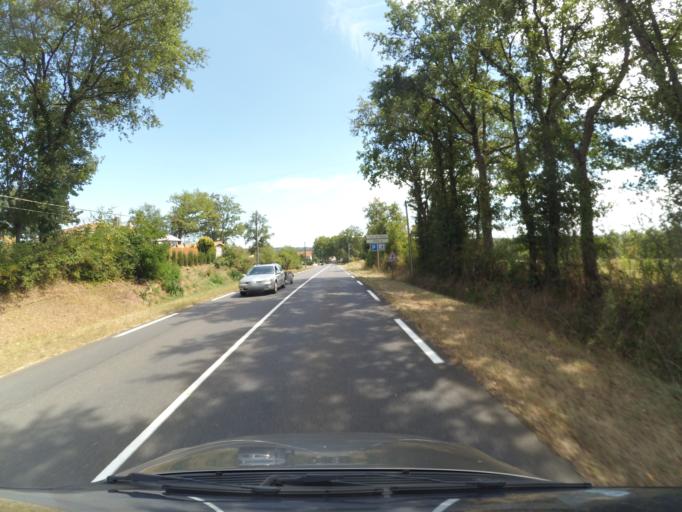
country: FR
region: Poitou-Charentes
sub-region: Departement de la Charente
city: Etagnac
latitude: 45.9360
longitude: 0.7354
